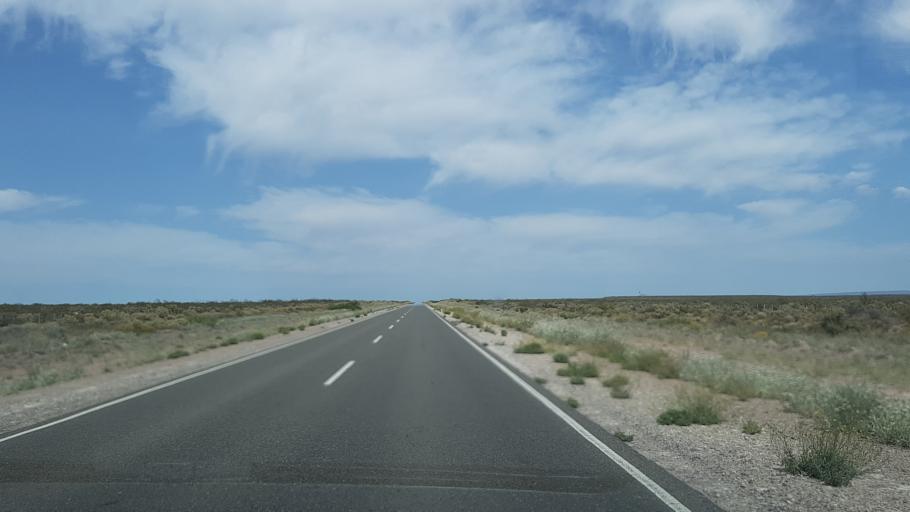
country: AR
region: Neuquen
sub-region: Departamento de Picun Leufu
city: Picun Leufu
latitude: -39.7513
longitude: -69.6275
